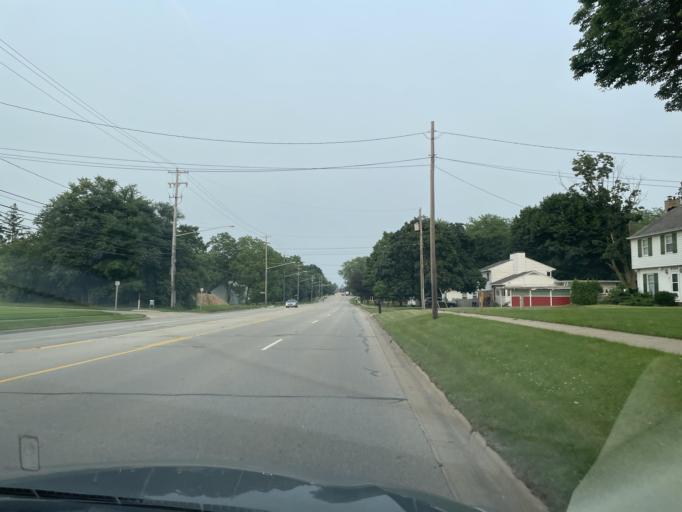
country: US
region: Michigan
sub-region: Kent County
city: Walker
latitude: 42.9717
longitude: -85.7353
